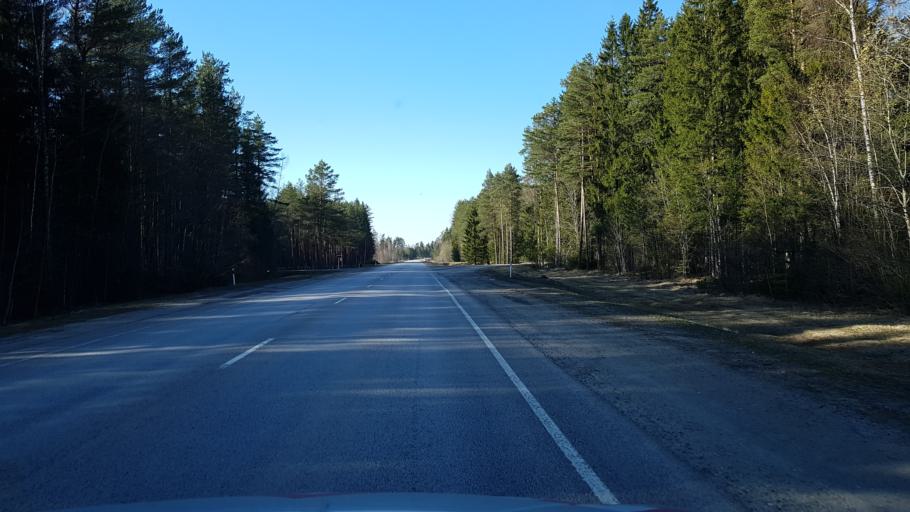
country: EE
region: Ida-Virumaa
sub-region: Johvi vald
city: Johvi
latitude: 59.1552
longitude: 27.3578
